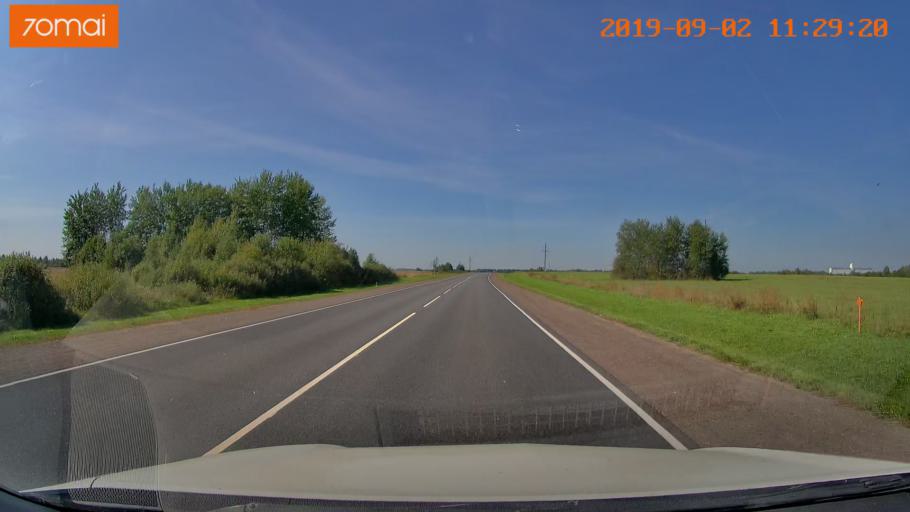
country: RU
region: Smolensk
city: Roslavl'
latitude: 53.9891
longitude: 32.8652
